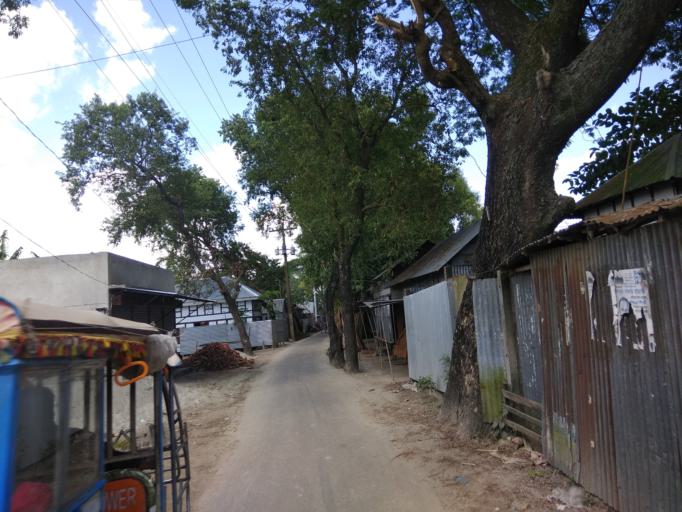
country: BD
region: Dhaka
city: Narayanganj
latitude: 23.4470
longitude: 90.4519
